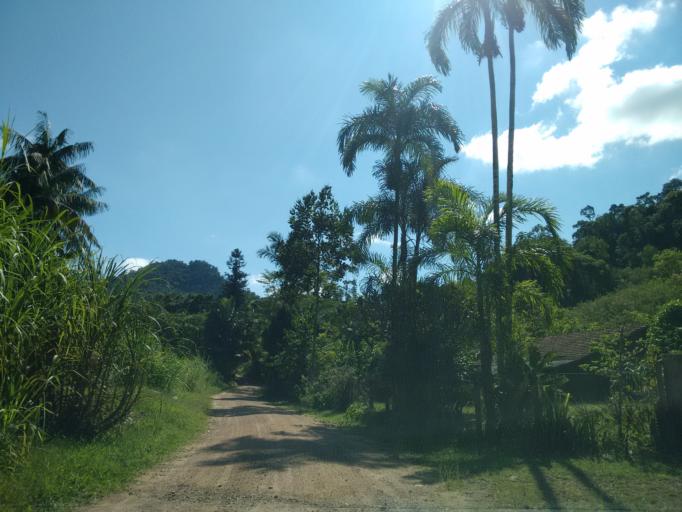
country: BR
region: Santa Catarina
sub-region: Indaial
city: Indaial
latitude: -26.9363
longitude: -49.1831
